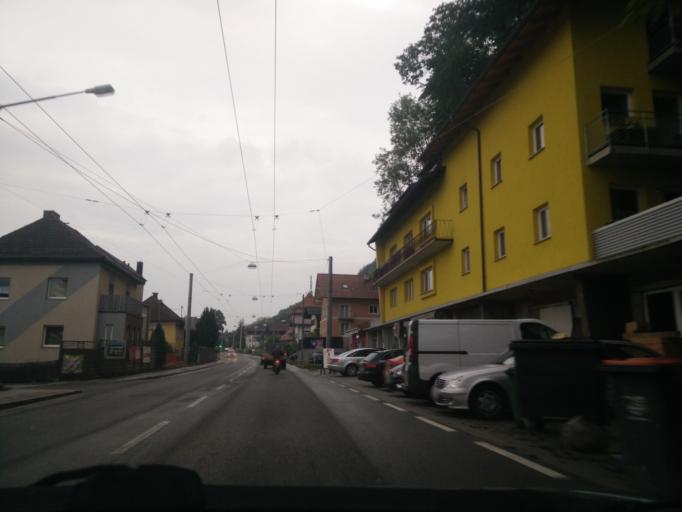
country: AT
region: Salzburg
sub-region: Politischer Bezirk Salzburg-Umgebung
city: Hallwang
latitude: 47.8206
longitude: 13.0761
